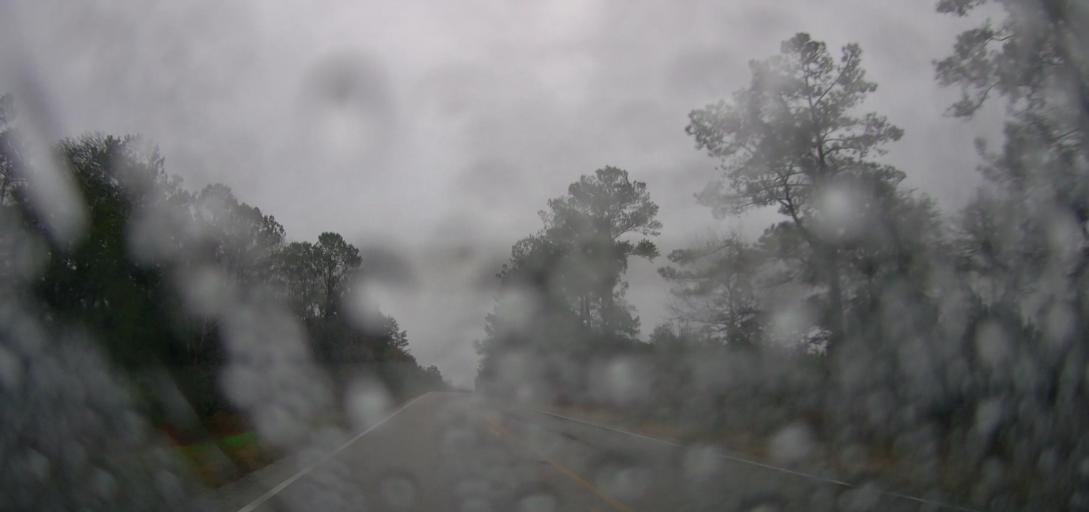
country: US
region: Alabama
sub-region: Autauga County
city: Pine Level
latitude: 32.5207
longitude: -86.6099
